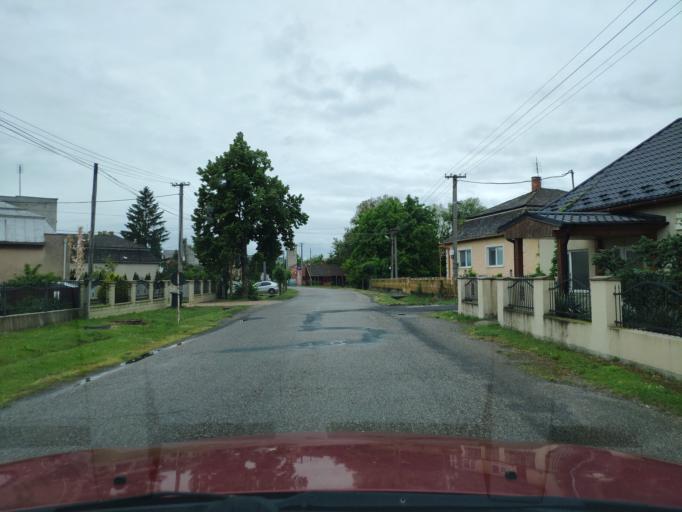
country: HU
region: Borsod-Abauj-Zemplen
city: Karcsa
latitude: 48.4003
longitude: 21.8088
